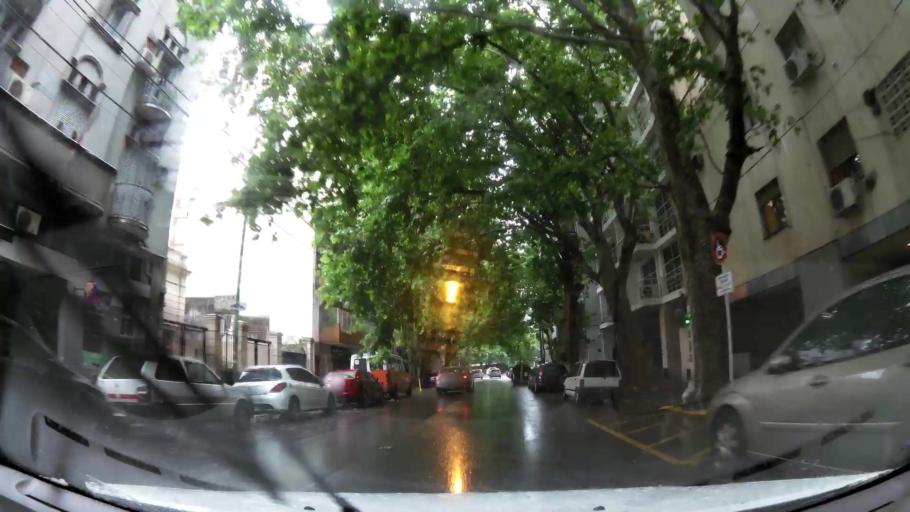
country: AR
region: Buenos Aires F.D.
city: Colegiales
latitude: -34.5762
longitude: -58.4232
